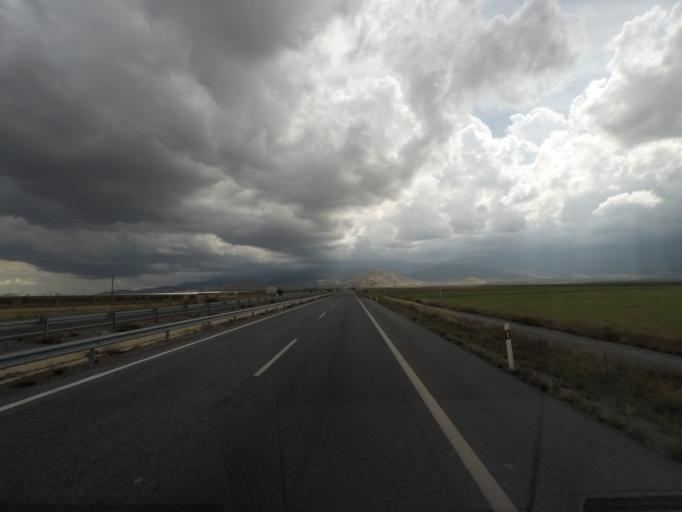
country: ES
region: Andalusia
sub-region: Provincia de Granada
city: Alquife
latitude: 37.2212
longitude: -3.0772
